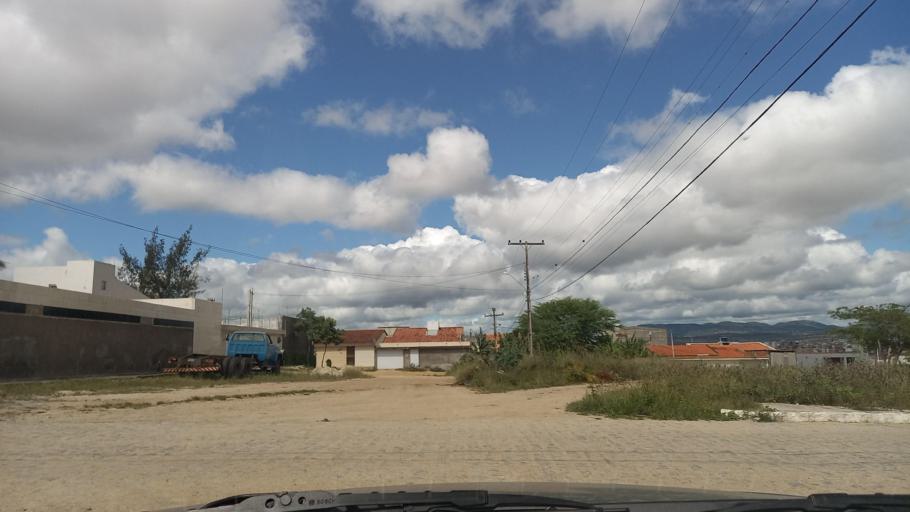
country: BR
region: Pernambuco
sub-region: Caruaru
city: Caruaru
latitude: -8.2575
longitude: -35.9811
